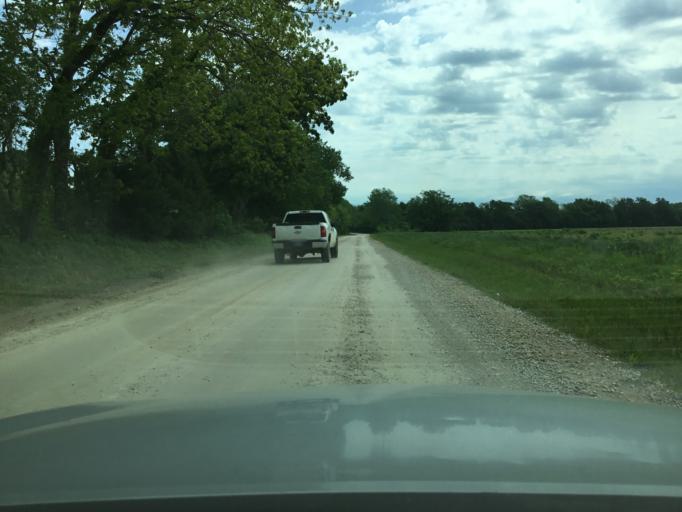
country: US
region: Kansas
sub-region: Montgomery County
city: Coffeyville
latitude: 37.0047
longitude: -95.5975
